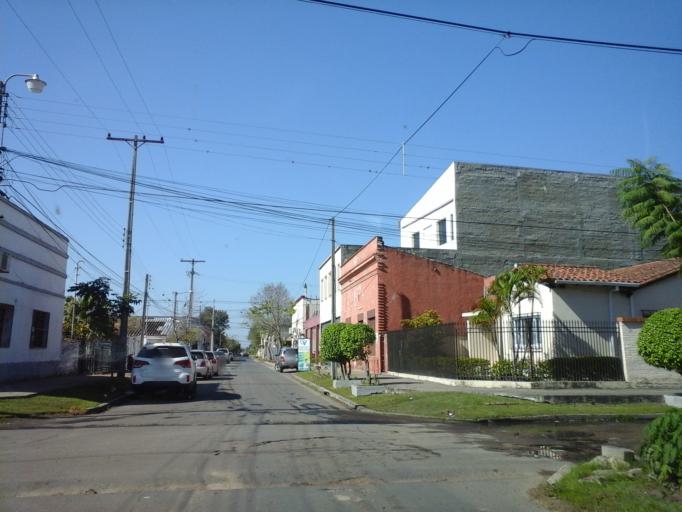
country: PY
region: Neembucu
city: Pilar
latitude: -26.8584
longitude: -58.3072
